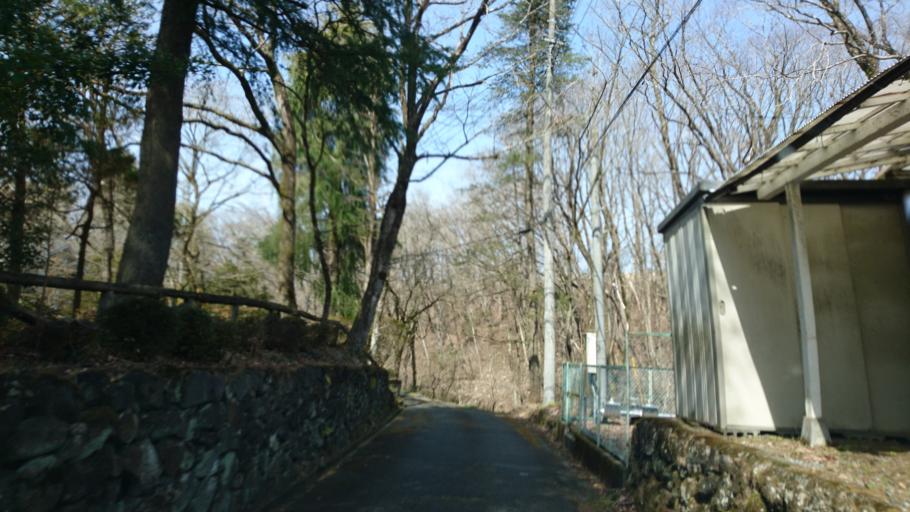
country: JP
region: Shizuoka
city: Fujinomiya
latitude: 35.3386
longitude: 138.5789
